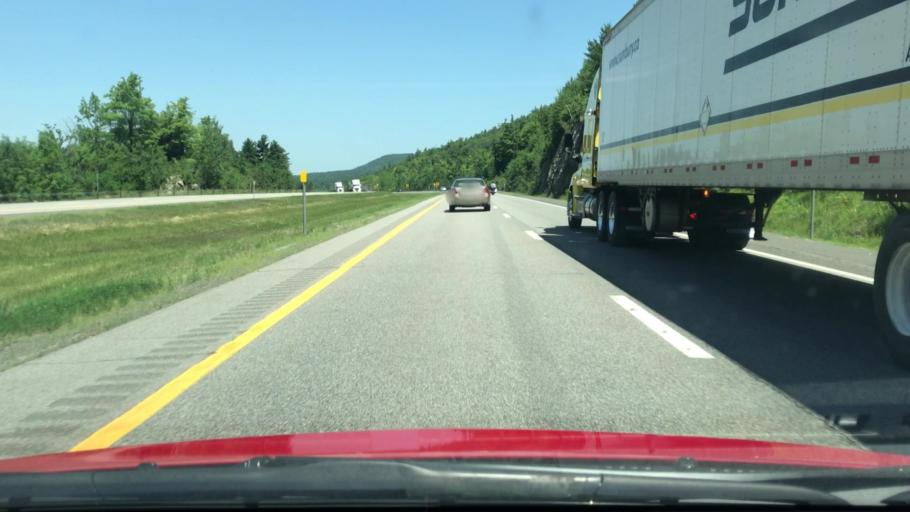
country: US
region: New York
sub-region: Essex County
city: Keeseville
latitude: 44.4079
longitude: -73.4981
